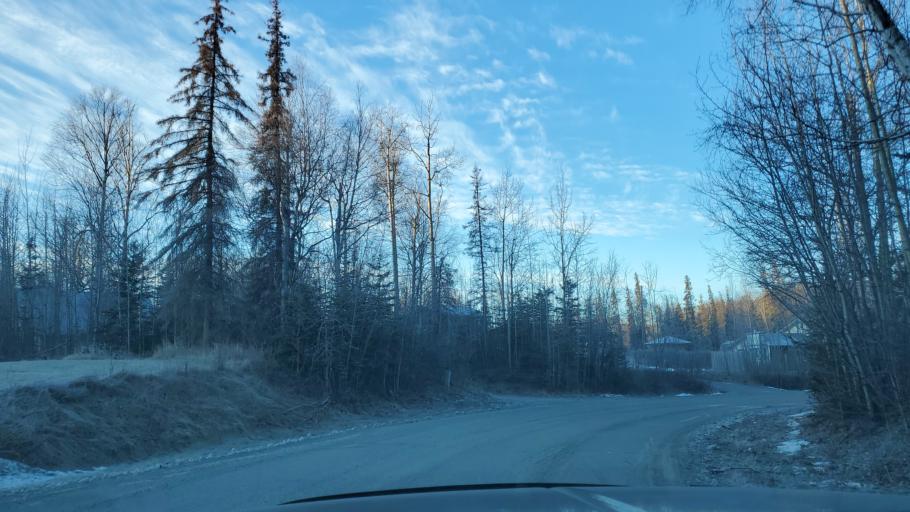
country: US
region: Alaska
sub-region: Matanuska-Susitna Borough
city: Tanaina
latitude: 61.6074
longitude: -149.4029
